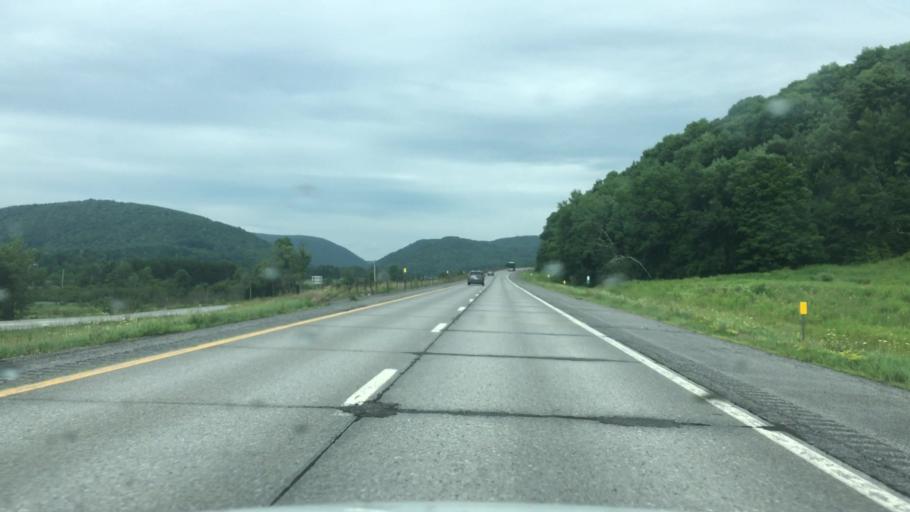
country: US
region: New York
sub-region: Otsego County
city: Worcester
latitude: 42.6102
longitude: -74.6813
